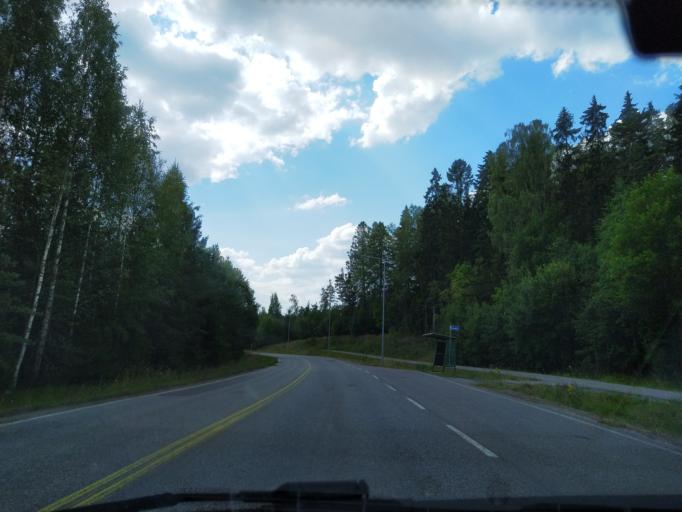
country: FI
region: Uusimaa
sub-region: Helsinki
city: Kirkkonummi
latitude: 60.1158
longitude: 24.4817
